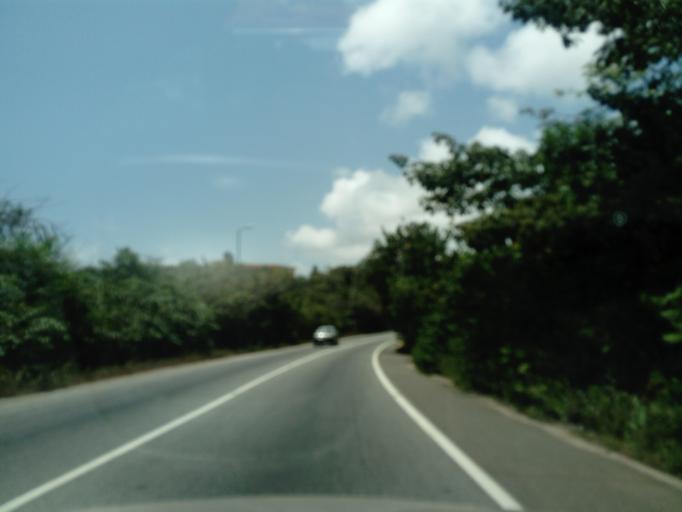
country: GH
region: Central
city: Cape Coast
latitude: 5.1255
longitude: -1.2427
